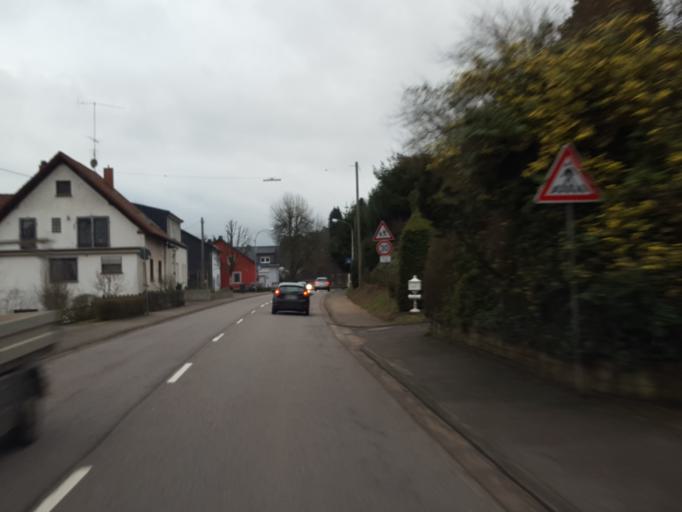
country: DE
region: Saarland
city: Beckingen
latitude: 49.4450
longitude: 6.7389
